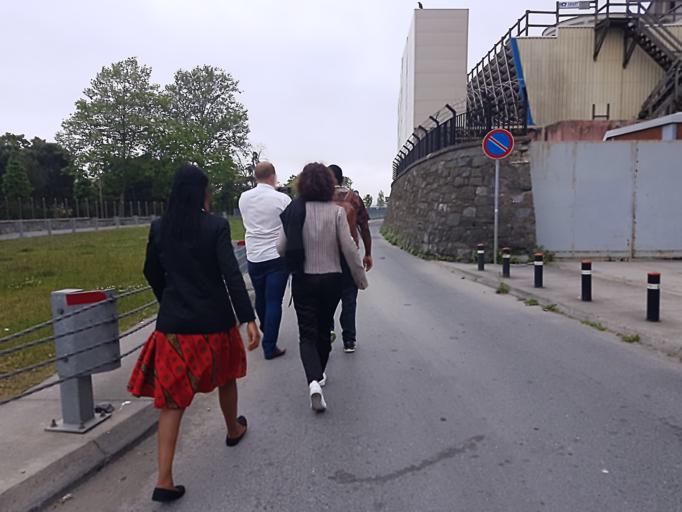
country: TR
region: Istanbul
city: Sisli
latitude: 41.0452
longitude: 28.9898
